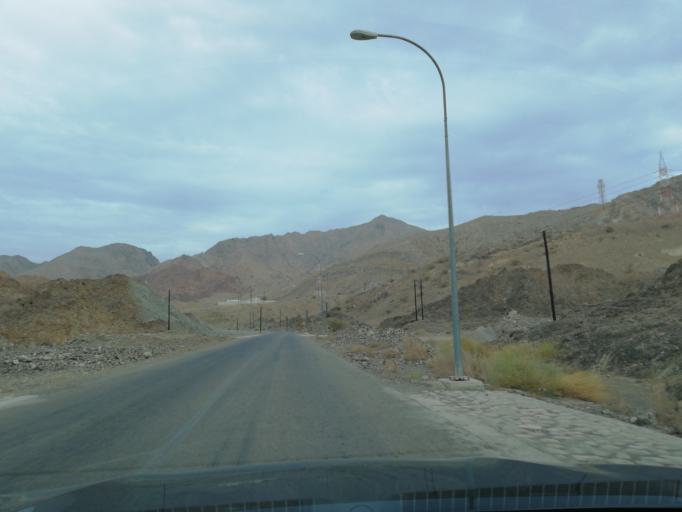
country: OM
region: Muhafazat Masqat
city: Bawshar
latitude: 23.4857
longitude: 58.3388
